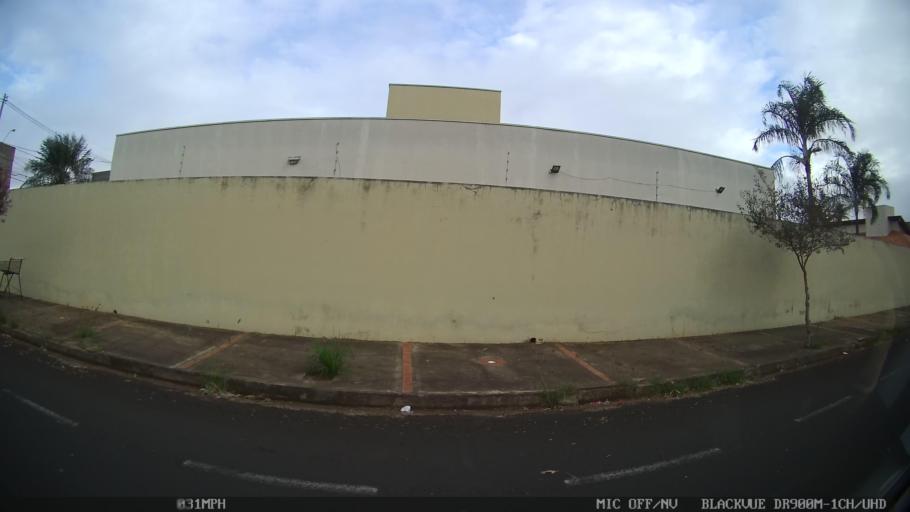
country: BR
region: Sao Paulo
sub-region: Sao Jose Do Rio Preto
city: Sao Jose do Rio Preto
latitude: -20.8417
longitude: -49.4006
